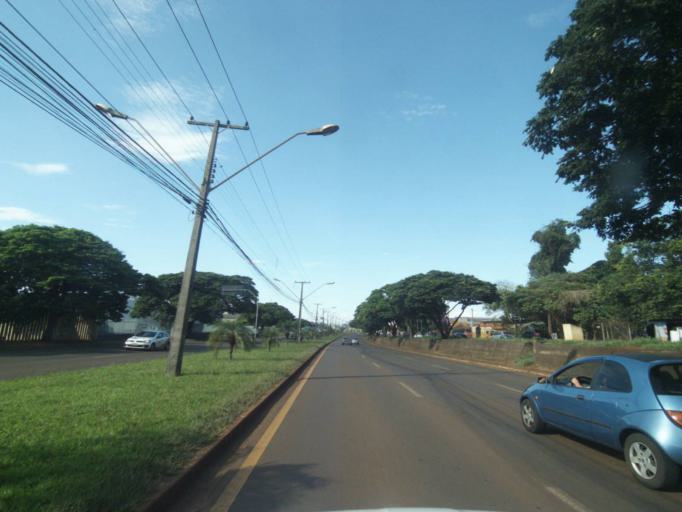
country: BR
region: Parana
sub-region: Londrina
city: Londrina
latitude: -23.3564
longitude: -51.1498
